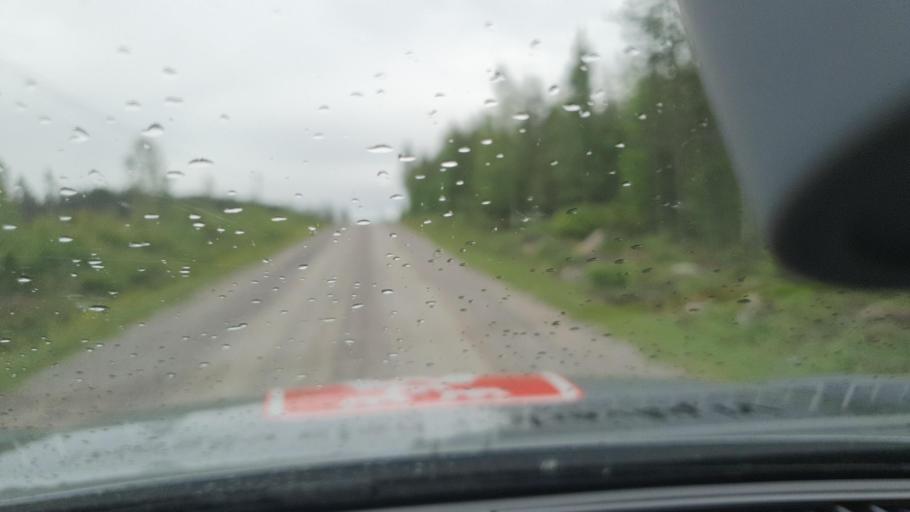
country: SE
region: Norrbotten
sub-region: Kalix Kommun
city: Rolfs
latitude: 66.0472
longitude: 23.0348
